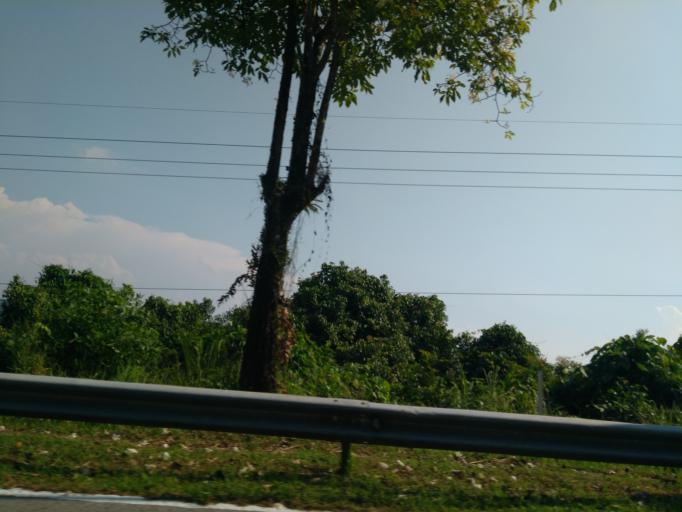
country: MY
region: Sarawak
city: Kuching
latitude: 1.7281
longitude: 110.3155
